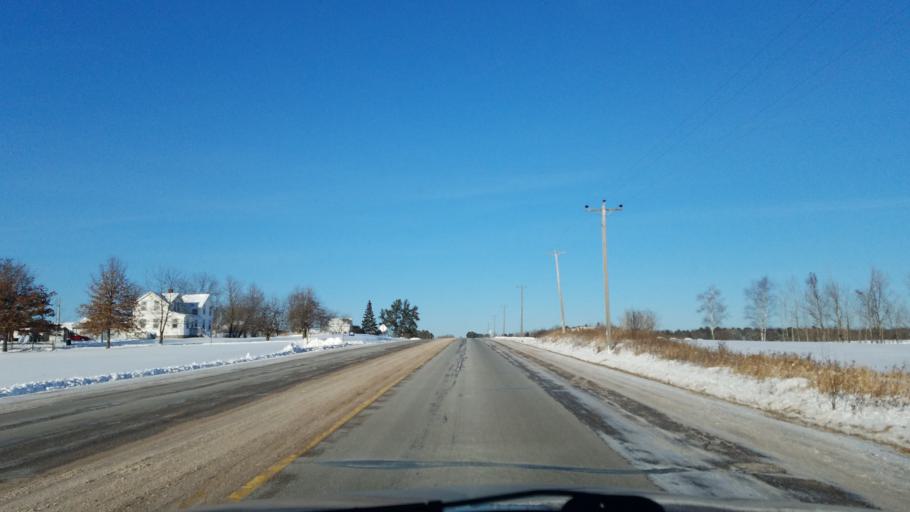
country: US
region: Wisconsin
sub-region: Barron County
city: Cumberland
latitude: 45.5158
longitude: -92.0520
